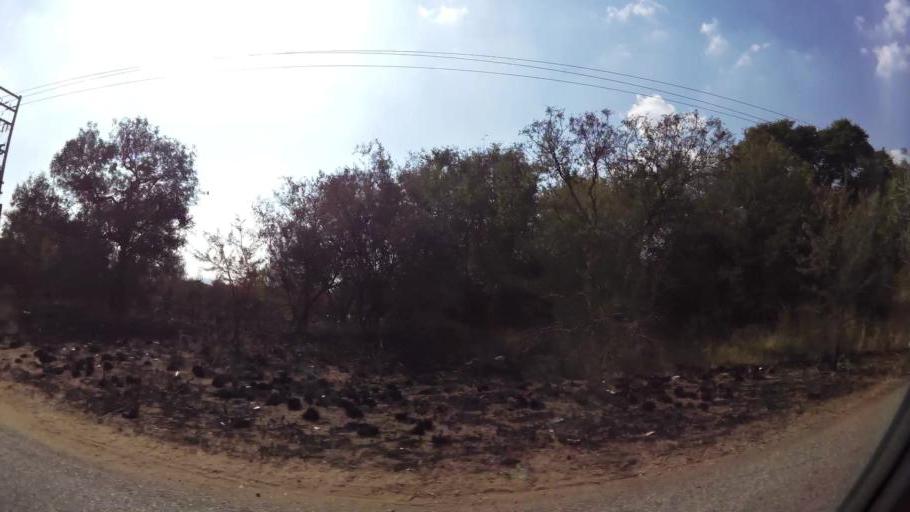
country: ZA
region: North-West
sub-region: Bojanala Platinum District Municipality
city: Rustenburg
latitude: -25.6342
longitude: 27.1595
